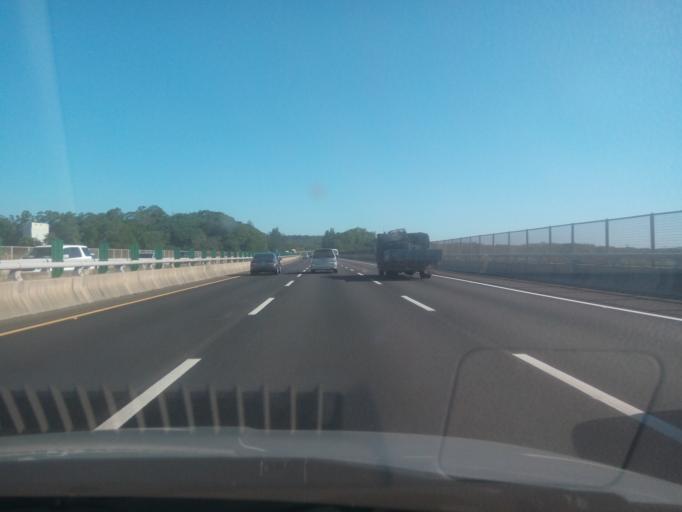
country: TW
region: Taiwan
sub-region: Hsinchu
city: Hsinchu
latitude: 24.7440
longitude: 120.9238
